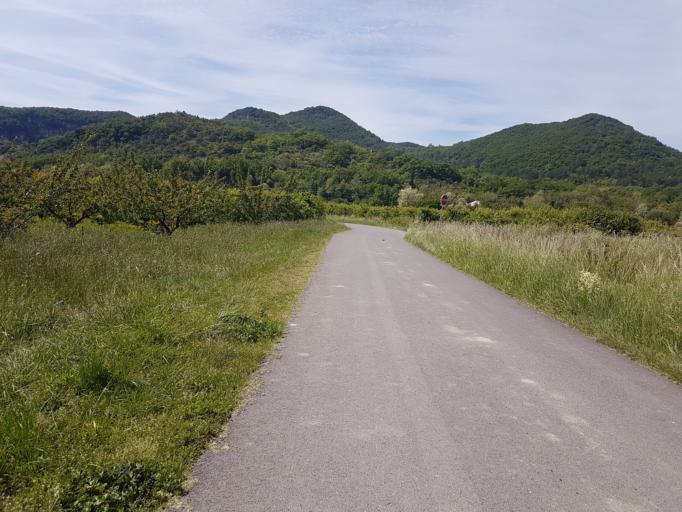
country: FR
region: Rhone-Alpes
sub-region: Departement de l'Ardeche
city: Le Pouzin
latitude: 44.7210
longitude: 4.7565
